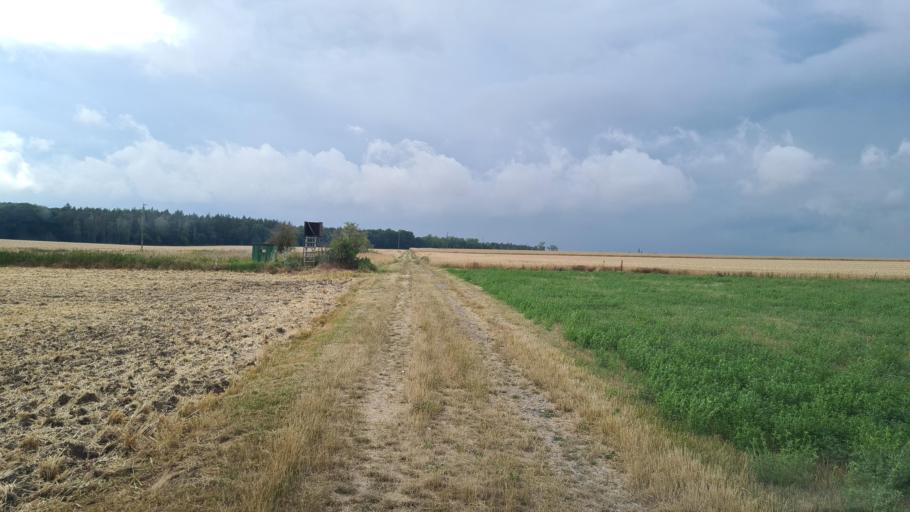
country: DE
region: Brandenburg
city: Juterbog
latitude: 51.9345
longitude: 13.1093
